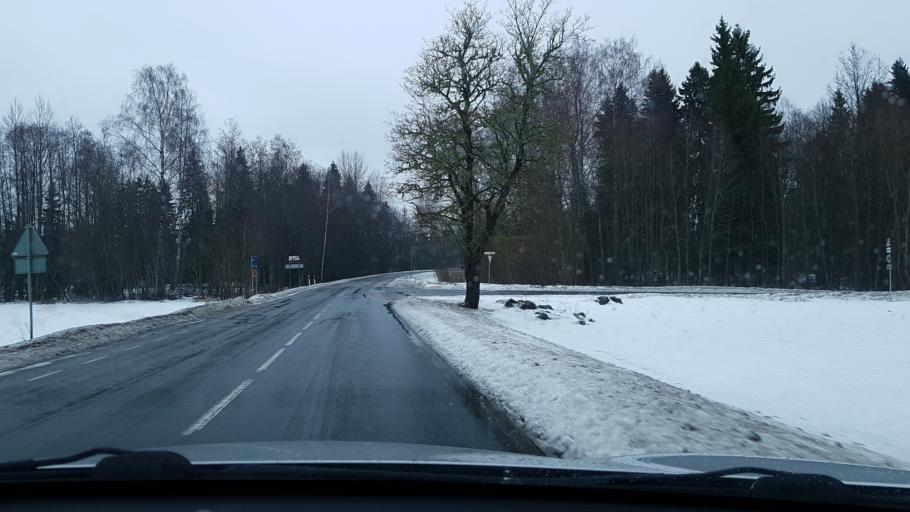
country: EE
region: Raplamaa
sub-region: Rapla vald
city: Rapla
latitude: 59.0143
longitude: 24.8089
